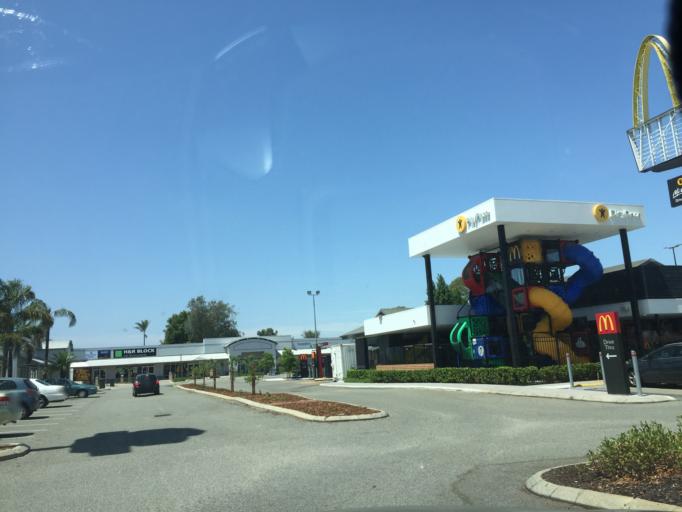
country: AU
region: Western Australia
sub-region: Canning
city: Ferndale
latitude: -32.0386
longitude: 115.9088
